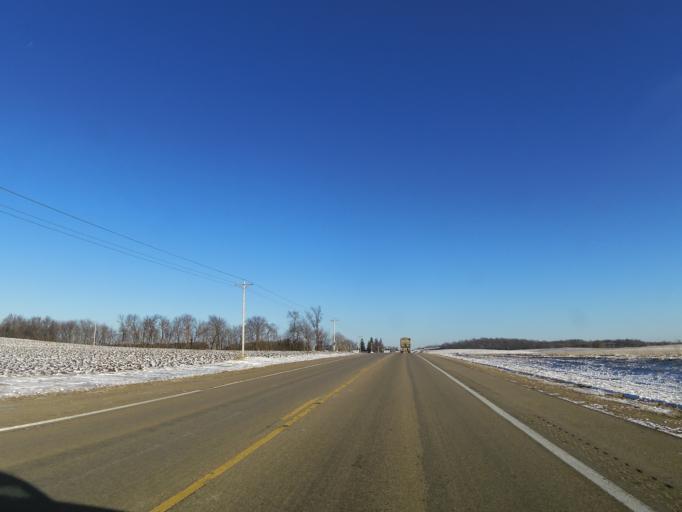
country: US
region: Minnesota
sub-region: Rice County
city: Lonsdale
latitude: 44.4861
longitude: -93.4669
